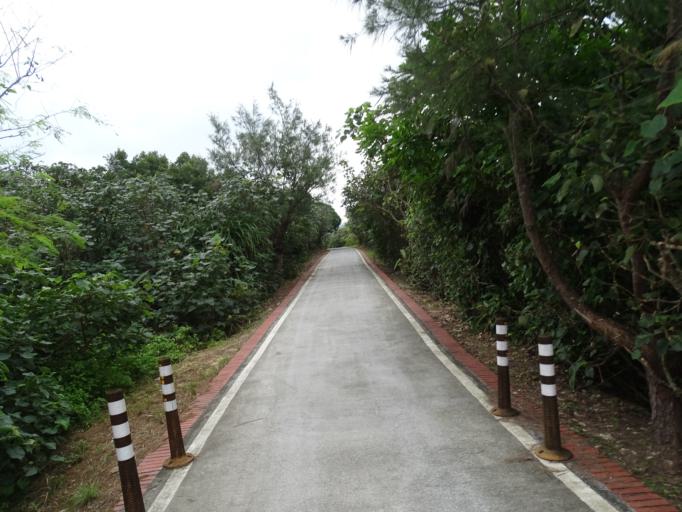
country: TW
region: Taiwan
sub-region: Keelung
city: Keelung
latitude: 25.0341
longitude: 121.9307
